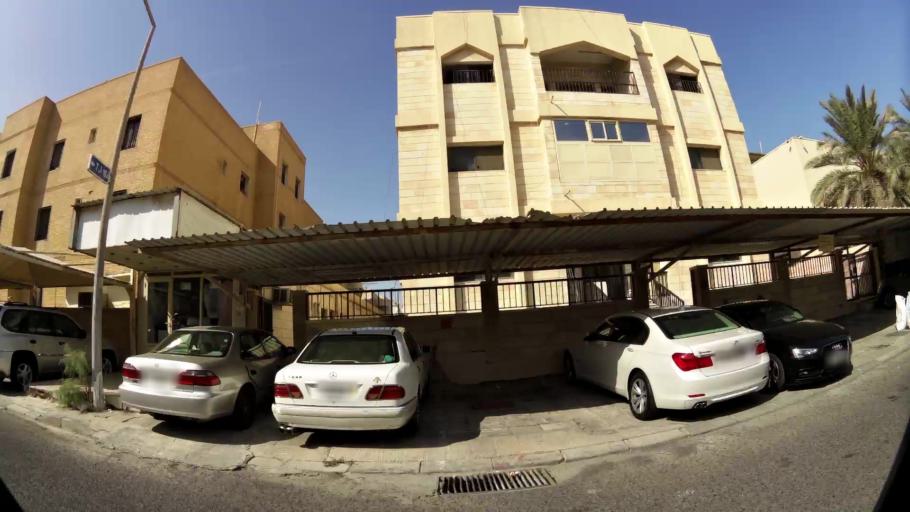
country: KW
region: Muhafazat Hawalli
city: Salwa
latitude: 29.2902
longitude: 48.0838
